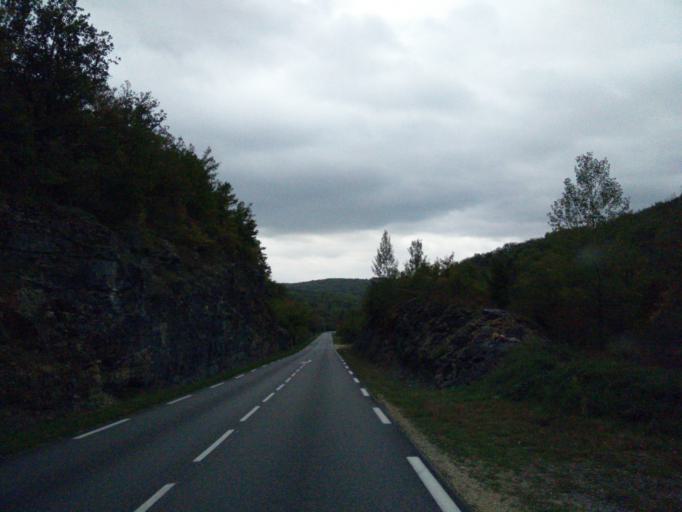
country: FR
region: Midi-Pyrenees
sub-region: Departement du Lot
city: Luzech
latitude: 44.5251
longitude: 1.3135
